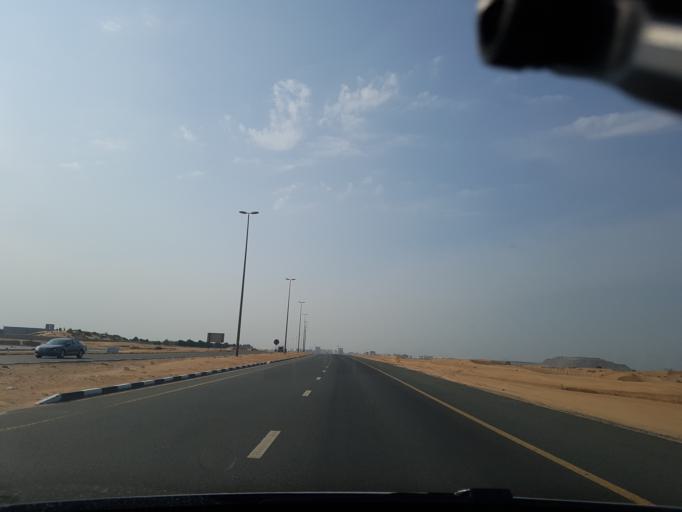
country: AE
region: Ajman
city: Ajman
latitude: 25.4095
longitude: 55.5702
